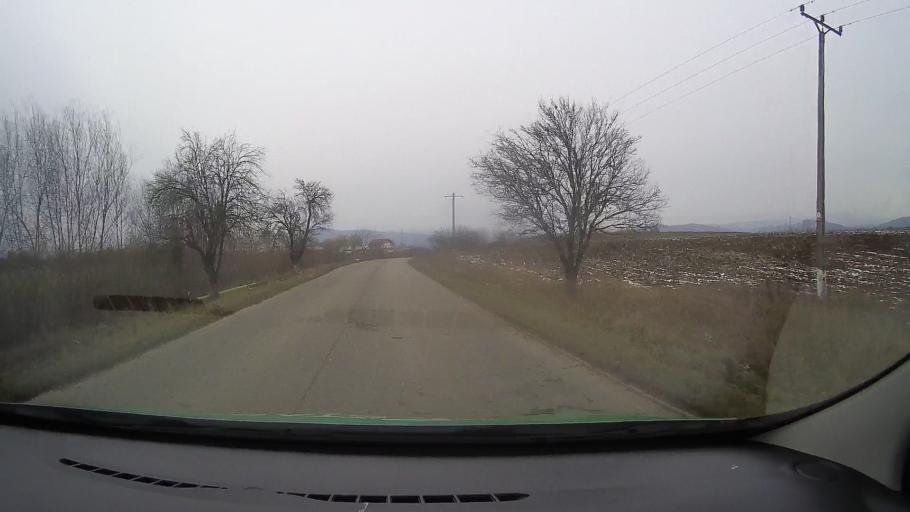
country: RO
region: Hunedoara
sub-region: Comuna Romos
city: Romos
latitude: 45.8755
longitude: 23.2643
